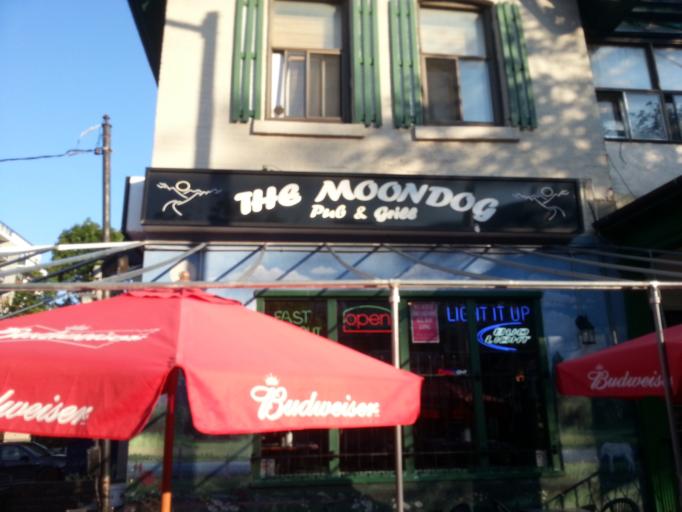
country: CA
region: Ontario
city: Ottawa
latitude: 45.4259
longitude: -75.6813
